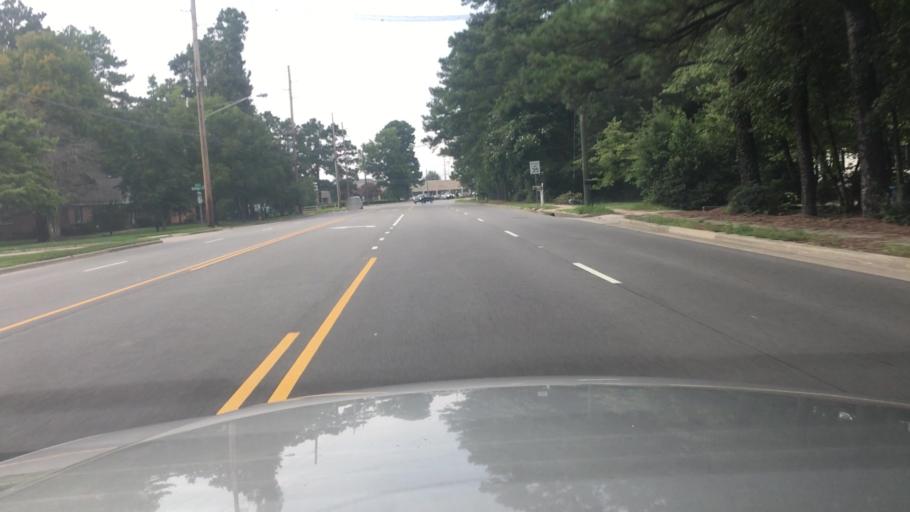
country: US
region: North Carolina
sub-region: Cumberland County
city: Fayetteville
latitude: 35.0628
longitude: -78.9502
